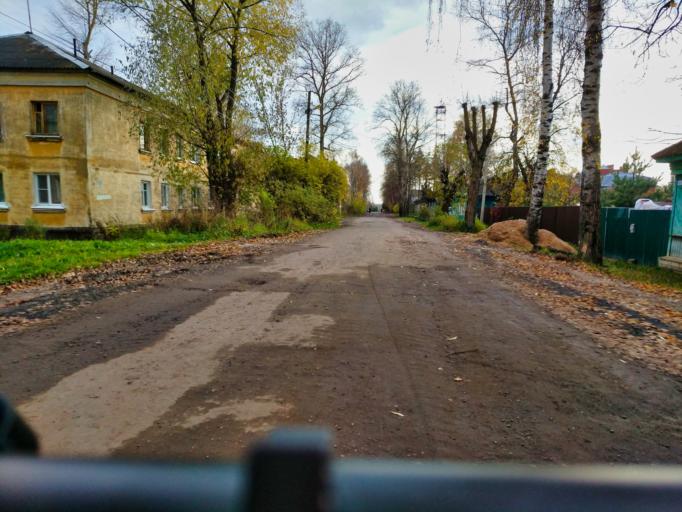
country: RU
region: Tverskaya
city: Rzhev
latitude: 56.2670
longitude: 34.3259
